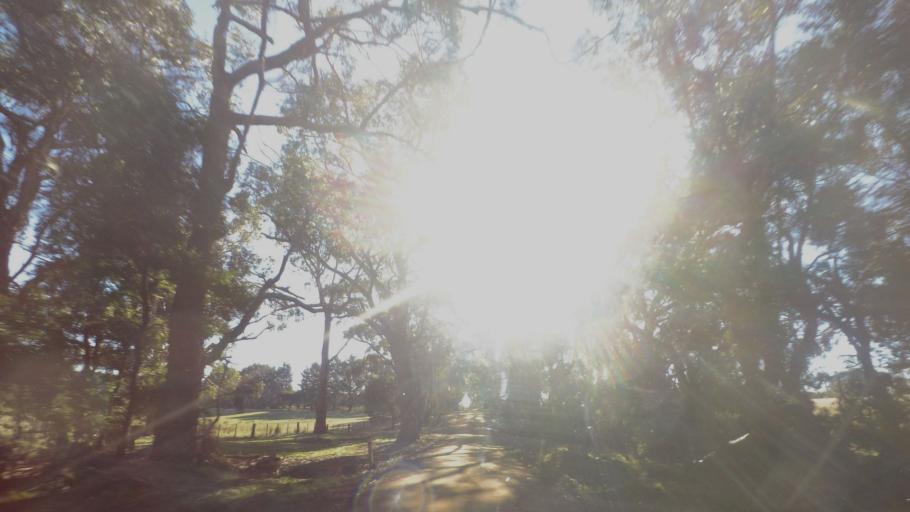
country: AU
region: Victoria
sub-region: Mount Alexander
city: Castlemaine
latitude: -37.2954
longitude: 144.3320
